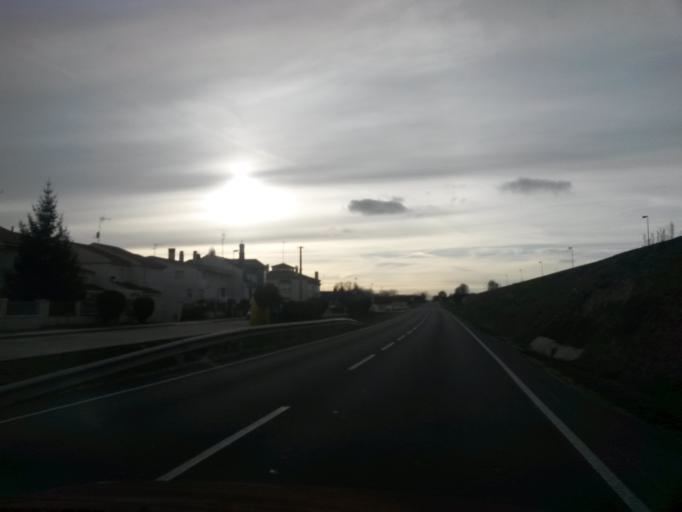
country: ES
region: Castille and Leon
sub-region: Provincia de Salamanca
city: Cabrerizos
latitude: 40.9742
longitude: -5.6144
